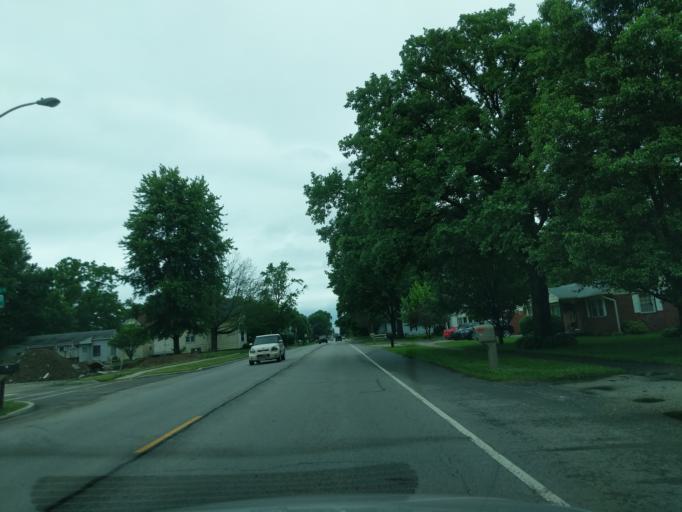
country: US
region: Indiana
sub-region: Hamilton County
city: Cicero
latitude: 40.1252
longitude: -86.0135
